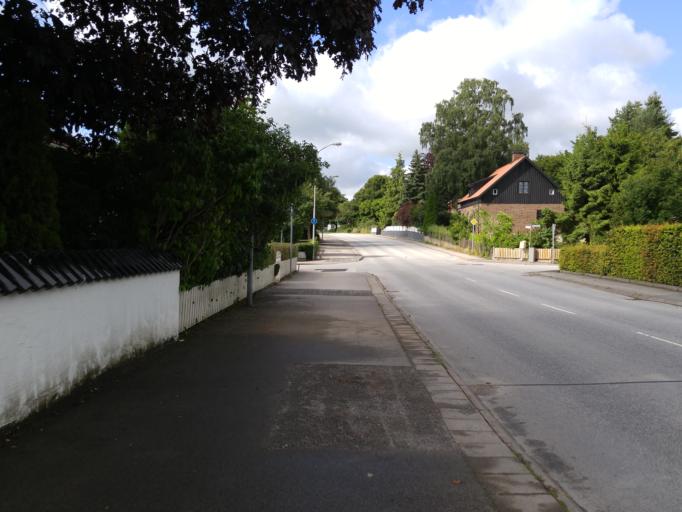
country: SE
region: Skane
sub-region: Hoors Kommun
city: Hoeoer
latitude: 55.9292
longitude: 13.5405
